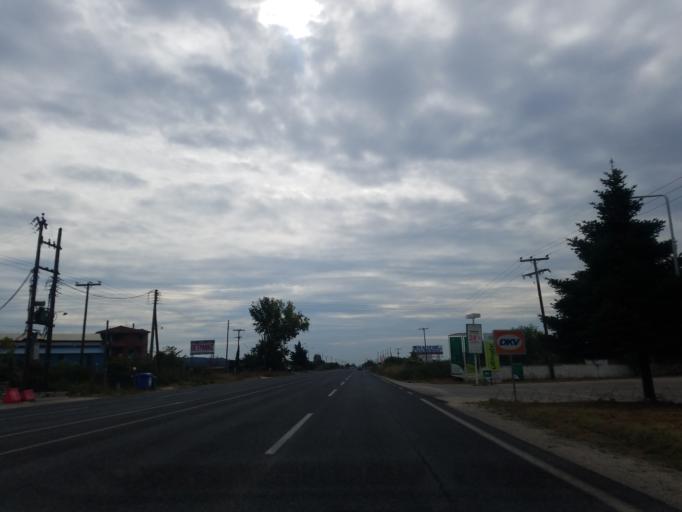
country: GR
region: Thessaly
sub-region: Trikala
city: Kalampaka
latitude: 39.6863
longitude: 21.6496
